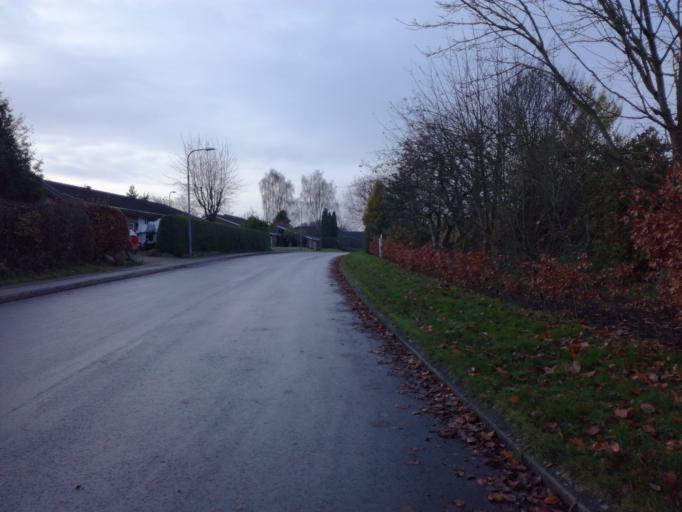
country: DK
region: South Denmark
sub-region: Vejle Kommune
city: Borkop
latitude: 55.6376
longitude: 9.6568
